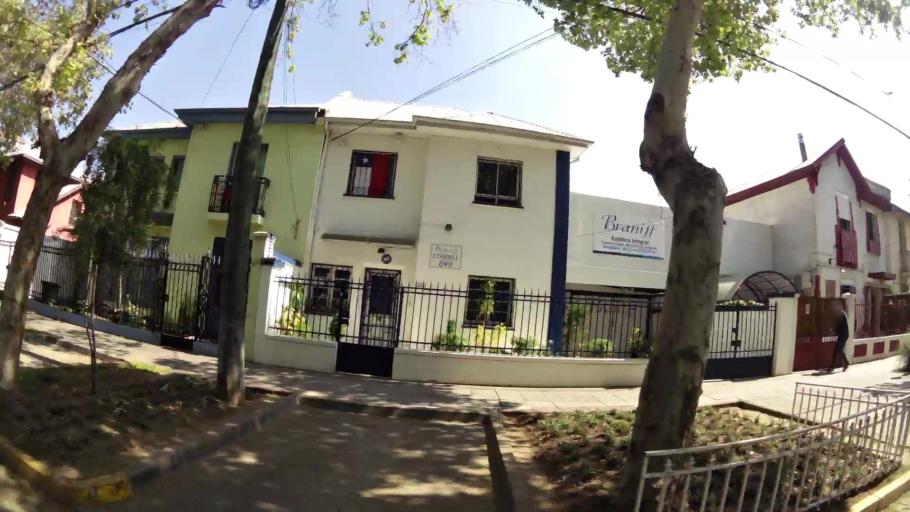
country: CL
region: Santiago Metropolitan
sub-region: Provincia de Santiago
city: Santiago
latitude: -33.4428
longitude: -70.6271
